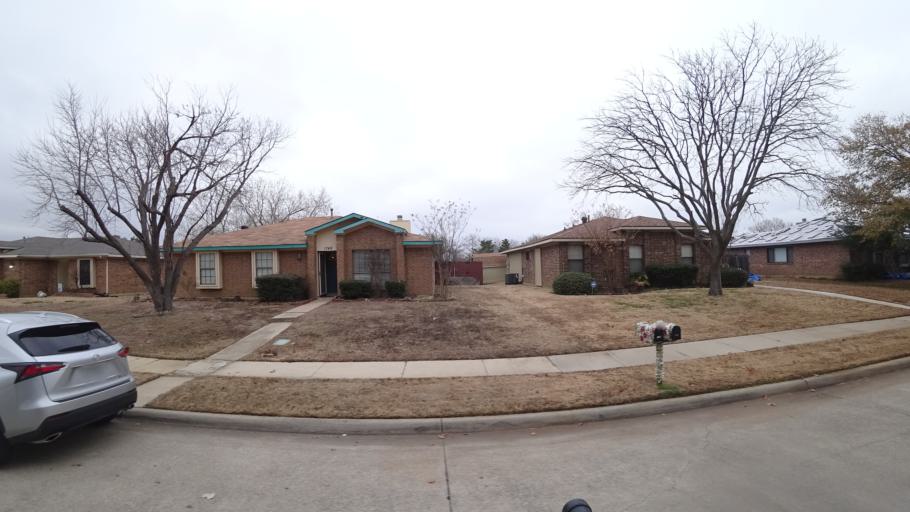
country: US
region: Texas
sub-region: Denton County
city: Highland Village
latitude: 33.0438
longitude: -97.0424
